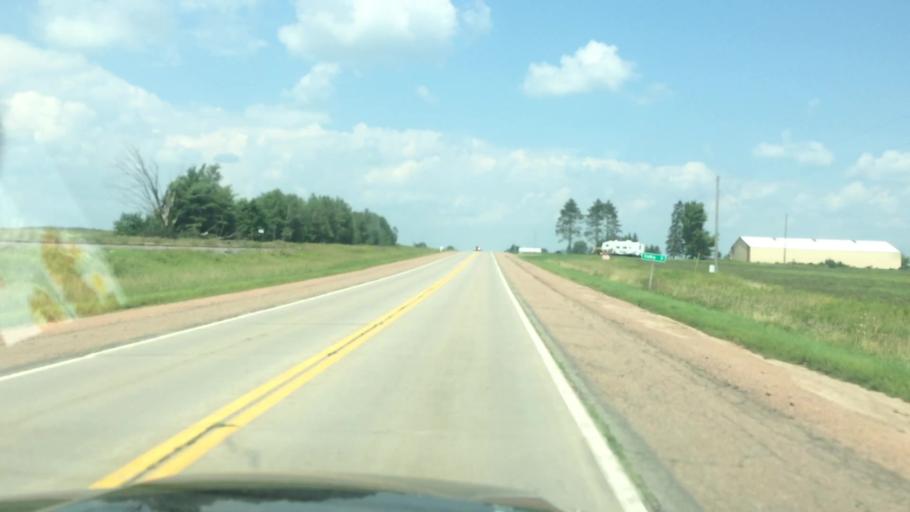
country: US
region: Wisconsin
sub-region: Clark County
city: Colby
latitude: 44.8593
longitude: -90.3158
